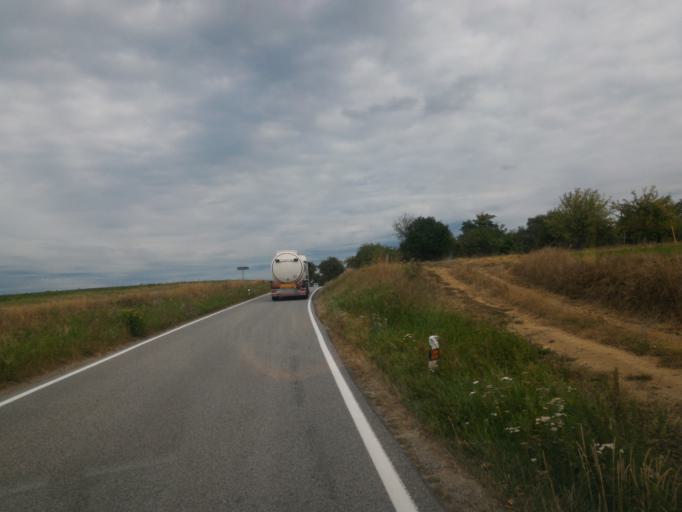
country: CZ
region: Vysocina
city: Zeletava
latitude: 49.1558
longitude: 15.5788
